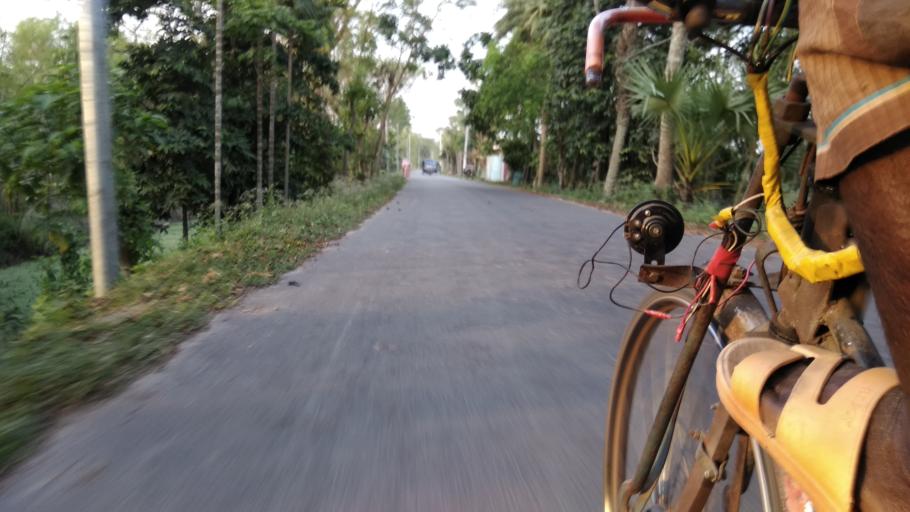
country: BD
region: Barisal
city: Mehendiganj
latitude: 22.9291
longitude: 90.4043
